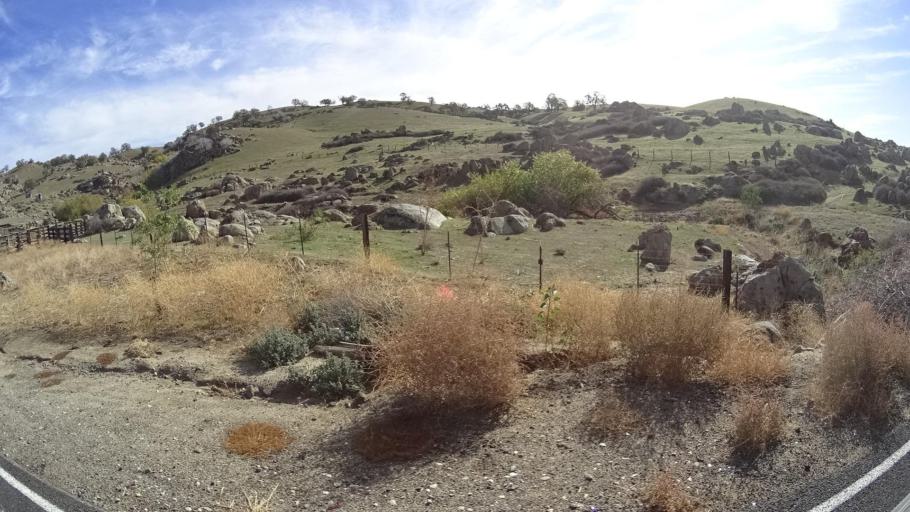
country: US
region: California
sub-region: Kern County
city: Oildale
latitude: 35.6131
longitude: -118.8593
